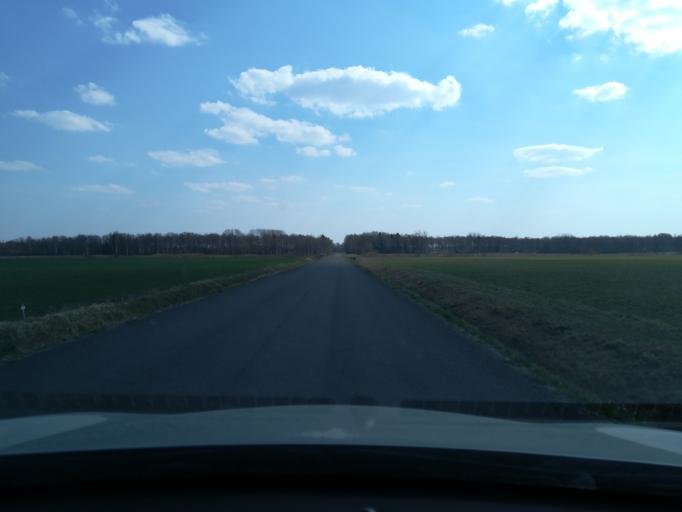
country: EE
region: Harju
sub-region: Saue linn
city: Saue
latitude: 59.3305
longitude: 24.5205
